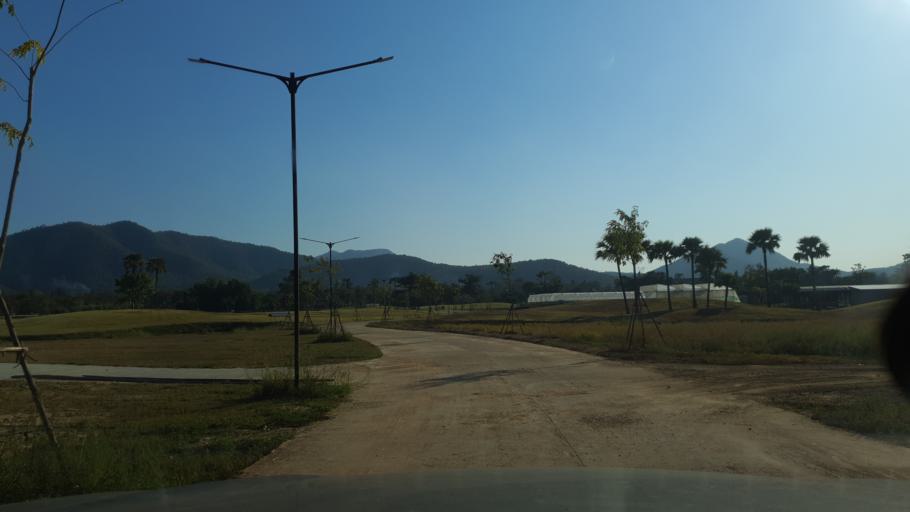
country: TH
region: Chiang Mai
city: Mae On
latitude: 18.7249
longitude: 99.2125
